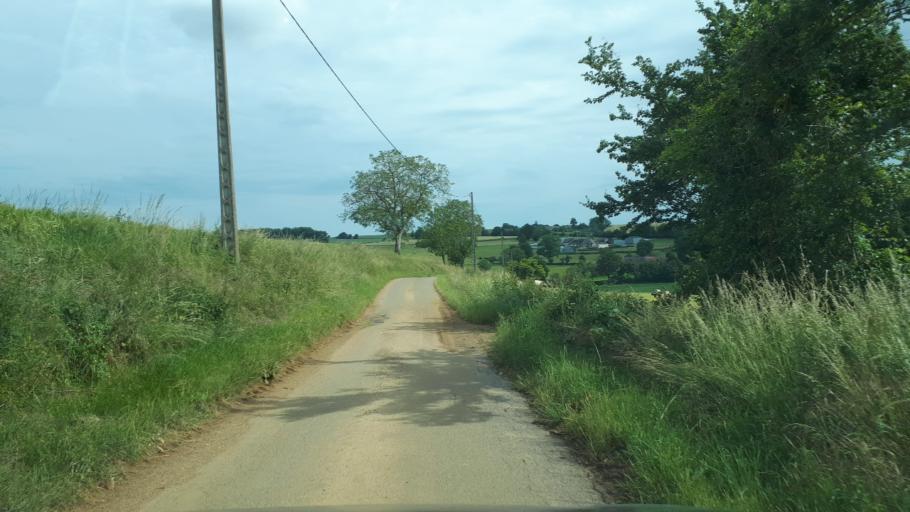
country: FR
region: Centre
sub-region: Departement du Cher
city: Sancerre
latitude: 47.3216
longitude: 2.7272
